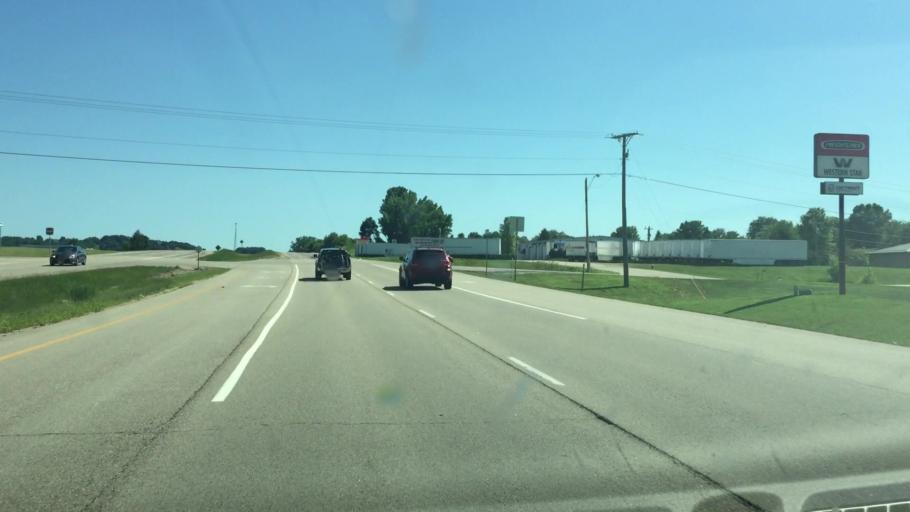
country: US
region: Iowa
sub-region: Dubuque County
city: Dubuque
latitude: 42.4483
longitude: -90.6803
